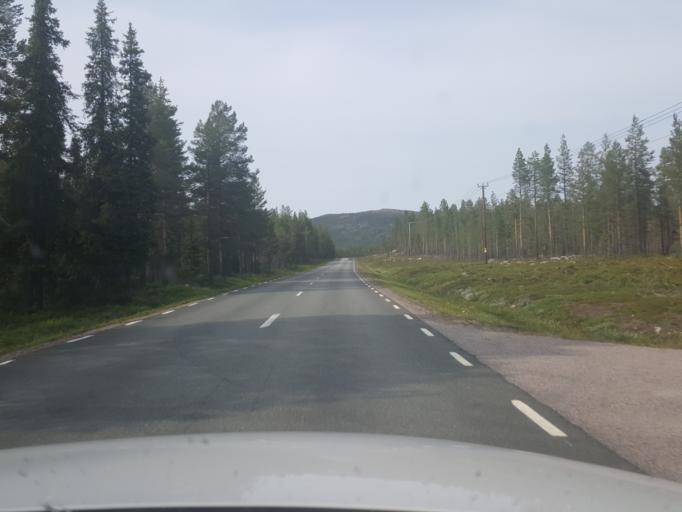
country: SE
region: Norrbotten
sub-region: Arjeplogs Kommun
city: Arjeplog
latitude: 65.8551
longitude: 18.0416
